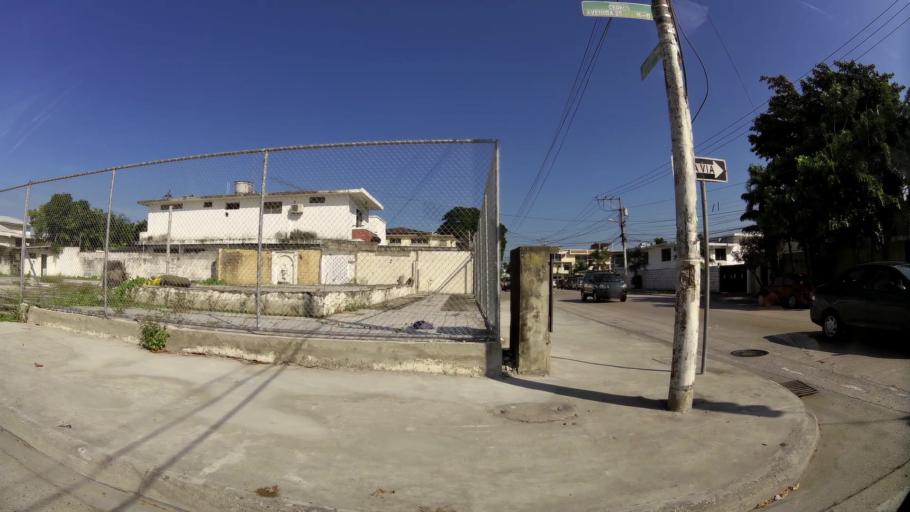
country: EC
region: Guayas
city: Guayaquil
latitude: -2.1688
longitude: -79.9042
